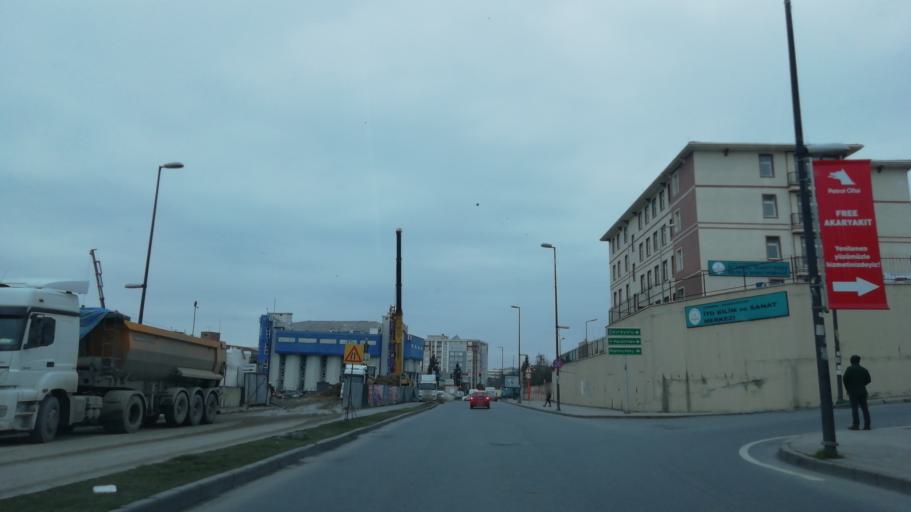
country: TR
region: Istanbul
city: Mahmutbey
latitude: 41.0140
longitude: 28.8182
